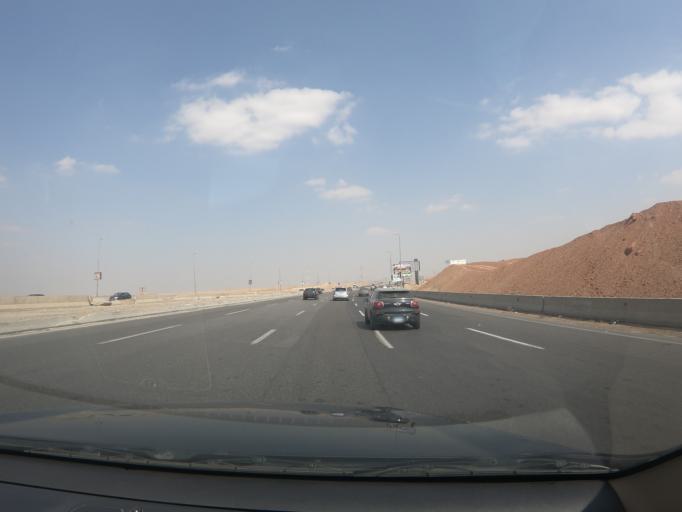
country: EG
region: Muhafazat al Qalyubiyah
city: Al Khankah
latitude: 30.0868
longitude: 31.5215
